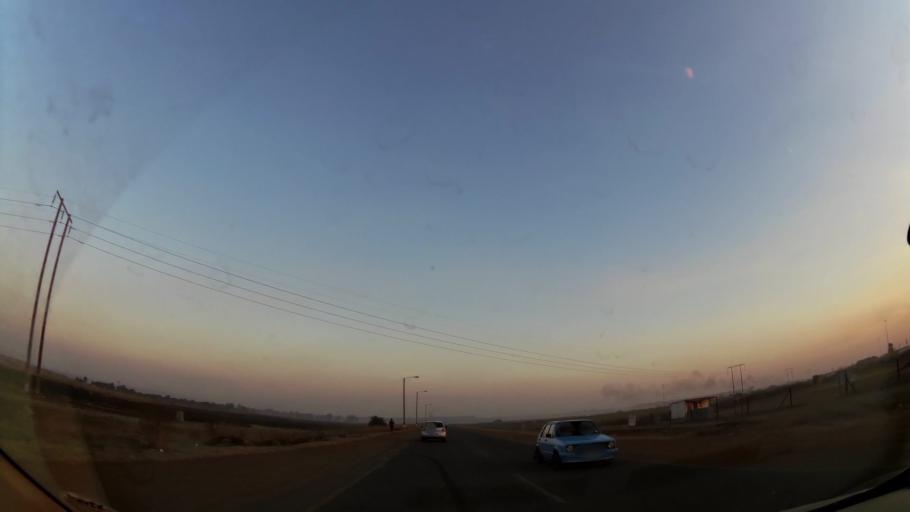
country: ZA
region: Gauteng
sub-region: Ekurhuleni Metropolitan Municipality
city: Springs
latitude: -26.3171
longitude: 28.4251
